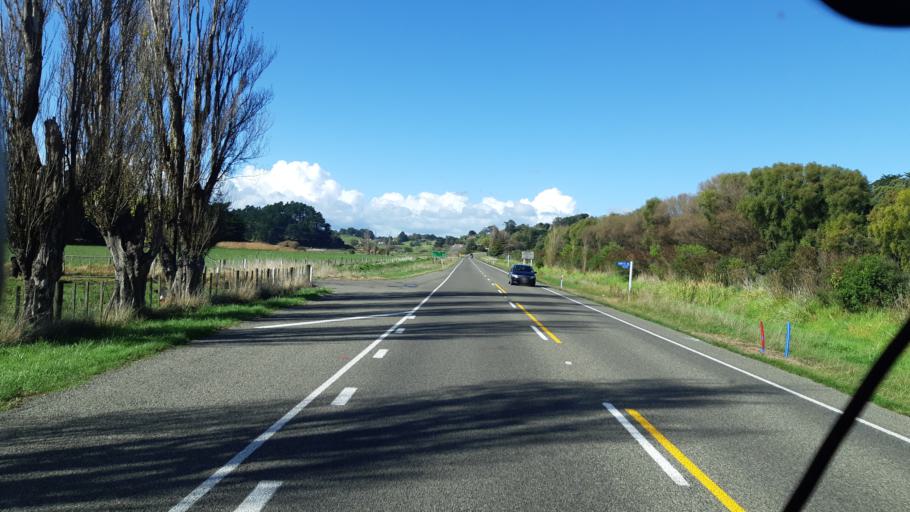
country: NZ
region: Manawatu-Wanganui
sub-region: Wanganui District
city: Wanganui
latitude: -39.9518
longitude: 175.0584
